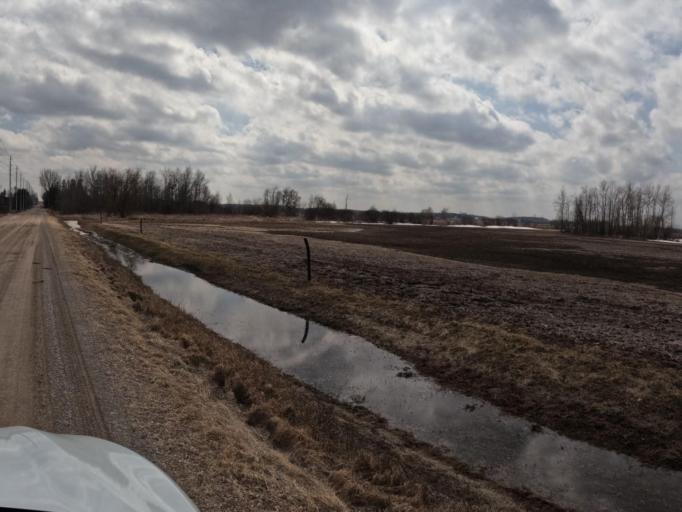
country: CA
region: Ontario
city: Shelburne
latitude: 44.0238
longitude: -80.3137
